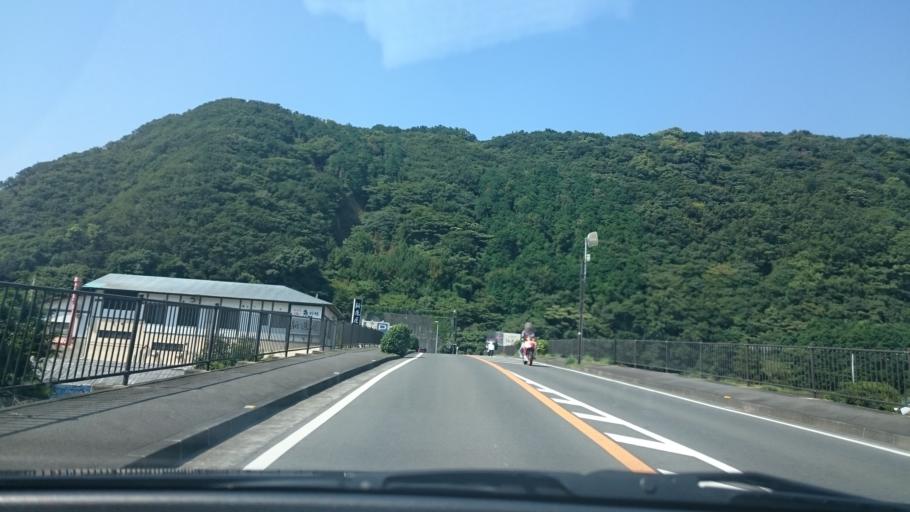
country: JP
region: Shizuoka
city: Heda
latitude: 34.8499
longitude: 138.7770
